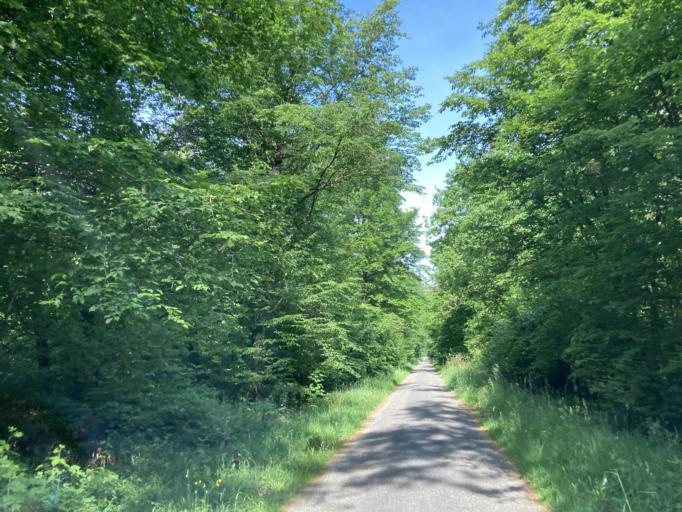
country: DE
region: Baden-Wuerttemberg
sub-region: Karlsruhe Region
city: Hambrucken
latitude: 49.2135
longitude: 8.5541
